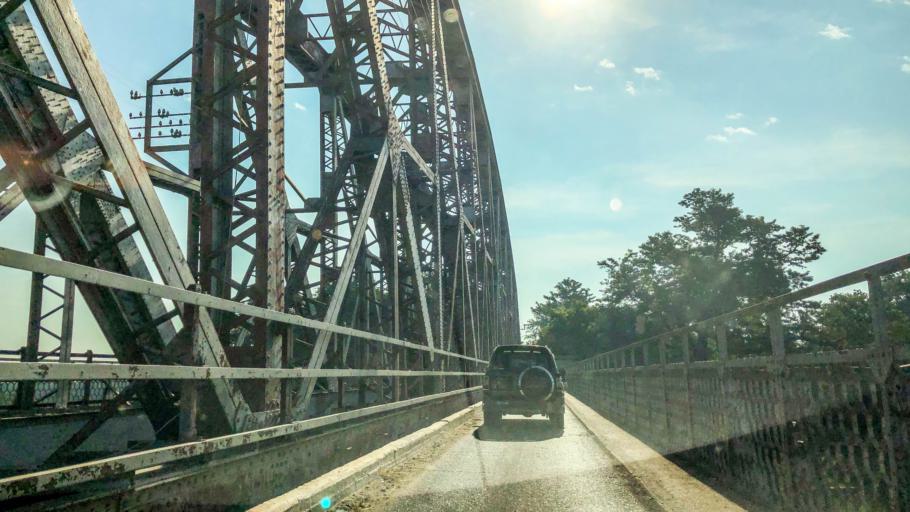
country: MM
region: Sagain
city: Sagaing
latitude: 21.8689
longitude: 95.9950
